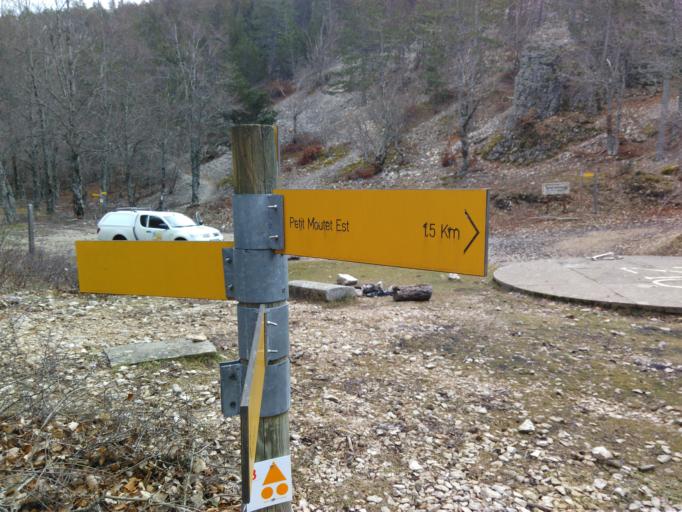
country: FR
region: Provence-Alpes-Cote d'Azur
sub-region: Departement du Vaucluse
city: Sault
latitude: 44.1369
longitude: 5.3184
